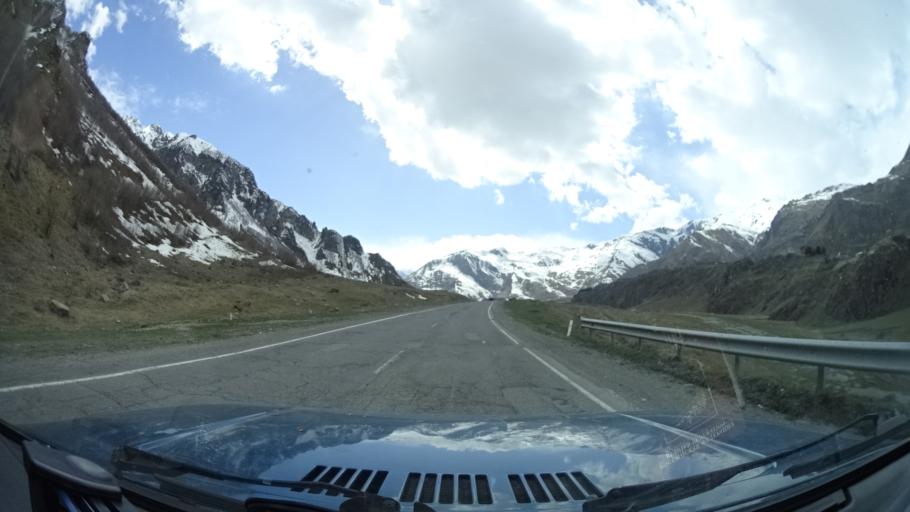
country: GE
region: Mtskheta-Mtianeti
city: Step'antsminda
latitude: 42.5965
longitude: 44.5684
